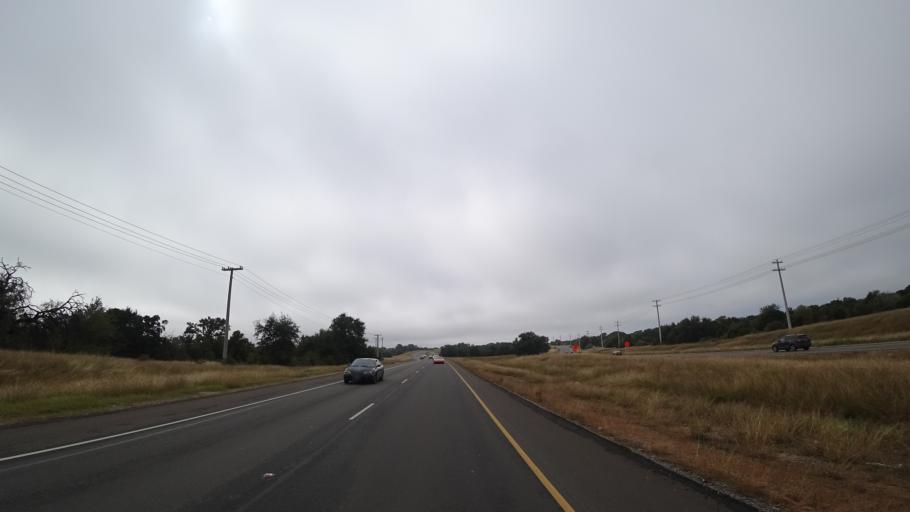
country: US
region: Texas
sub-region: Travis County
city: Shady Hollow
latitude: 30.1841
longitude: -97.8791
